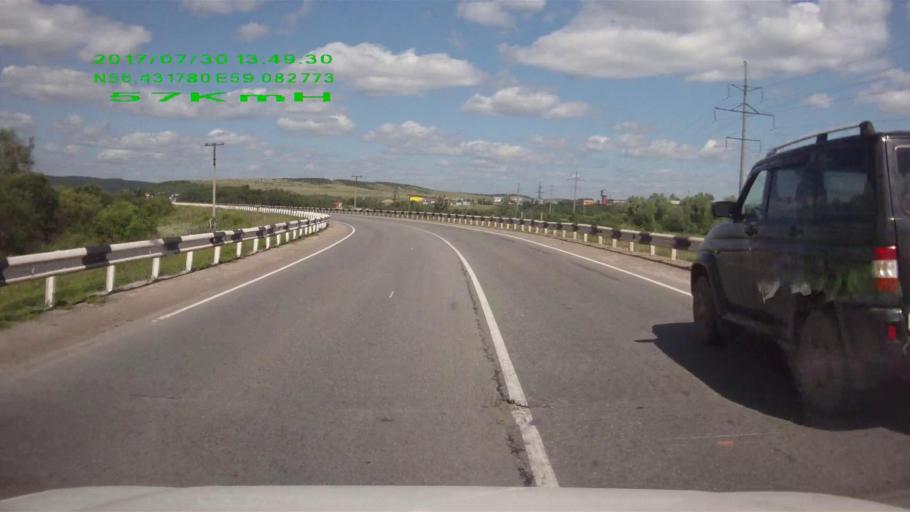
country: RU
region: Sverdlovsk
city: Mikhaylovsk
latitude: 56.4320
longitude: 59.0831
